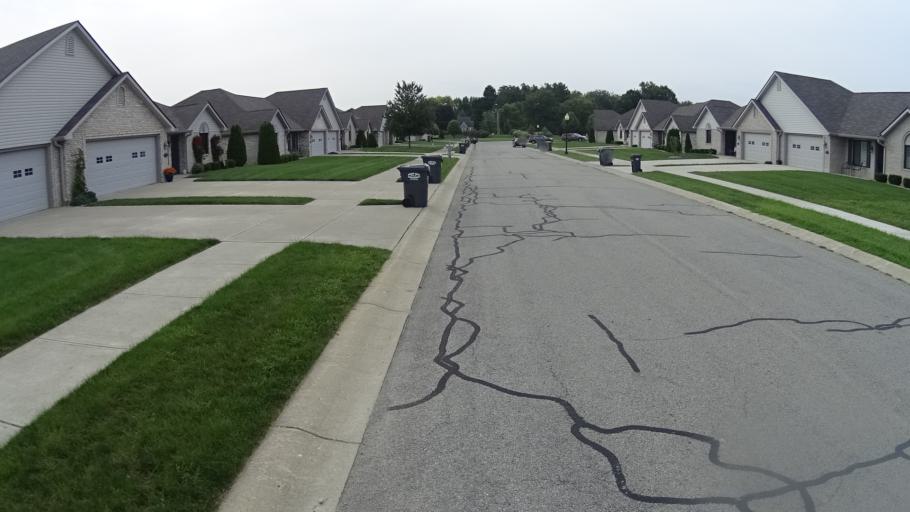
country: US
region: Indiana
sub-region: Madison County
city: Pendleton
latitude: 40.0301
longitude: -85.7297
